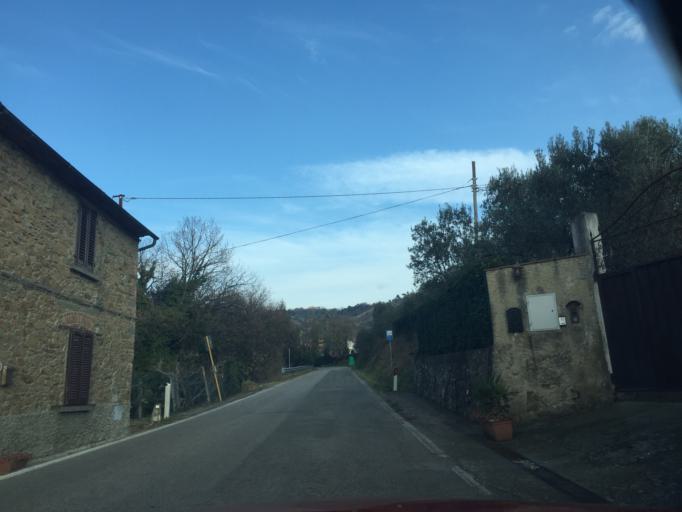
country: IT
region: Tuscany
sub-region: Province of Florence
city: Vinci
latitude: 43.8065
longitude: 10.9283
